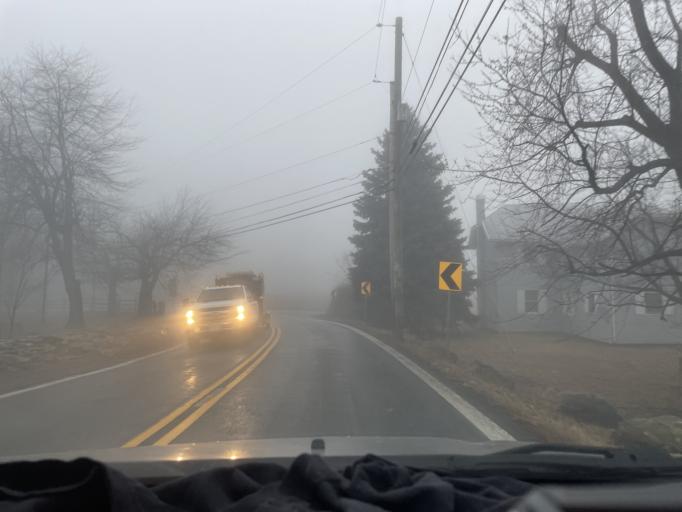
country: US
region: Maryland
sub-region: Washington County
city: Highfield-Cascade
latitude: 39.7040
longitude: -77.4858
